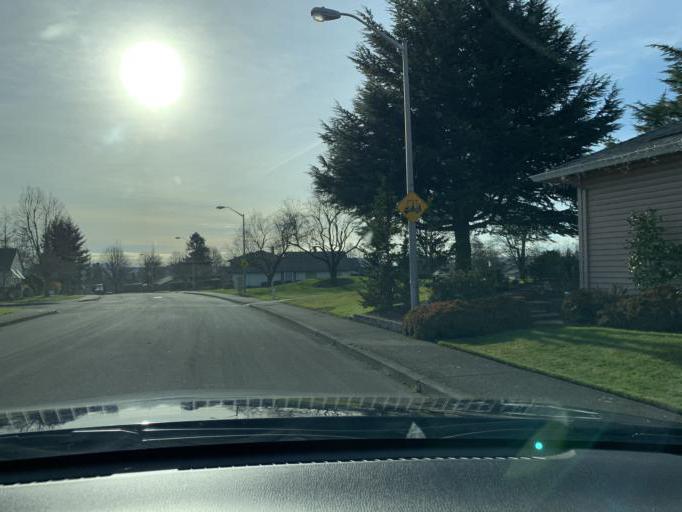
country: US
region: Washington
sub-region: Clark County
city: Mill Plain
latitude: 45.5966
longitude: -122.5120
